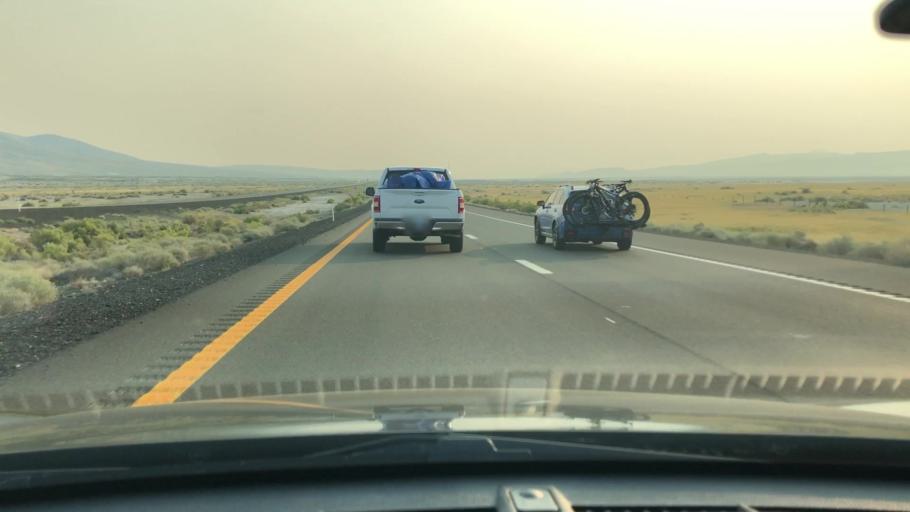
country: US
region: Nevada
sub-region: Lyon County
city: Fernley
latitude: 39.6478
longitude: -119.1691
